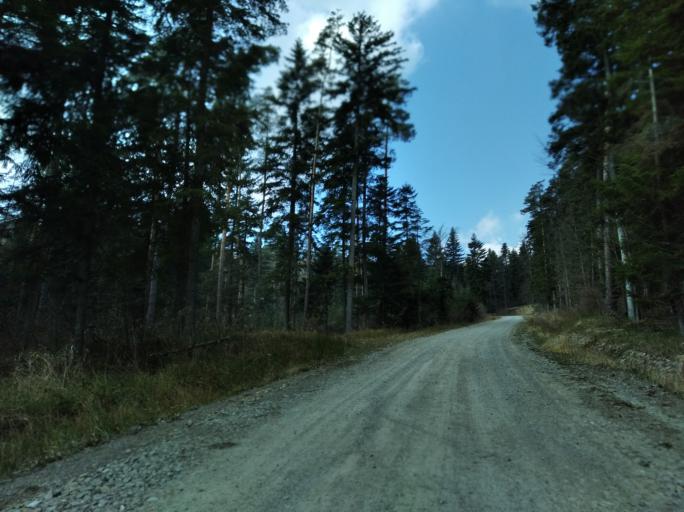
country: PL
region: Subcarpathian Voivodeship
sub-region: Powiat strzyzowski
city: Strzyzow
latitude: 49.8129
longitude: 21.8224
